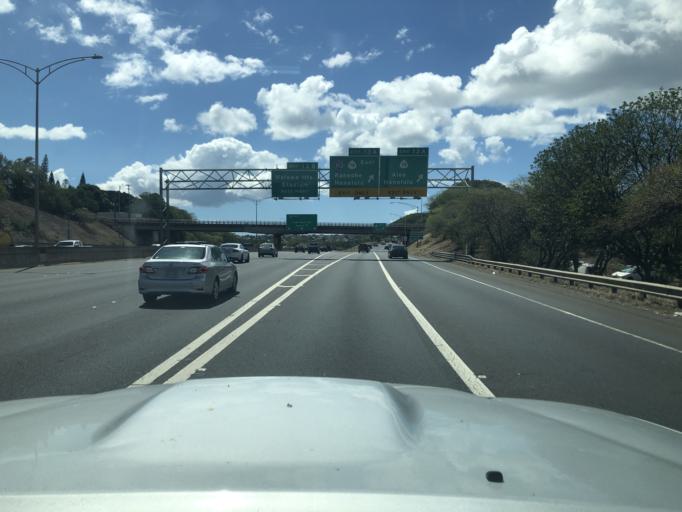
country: US
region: Hawaii
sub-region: Honolulu County
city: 'Aiea
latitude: 21.3784
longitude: -157.9282
